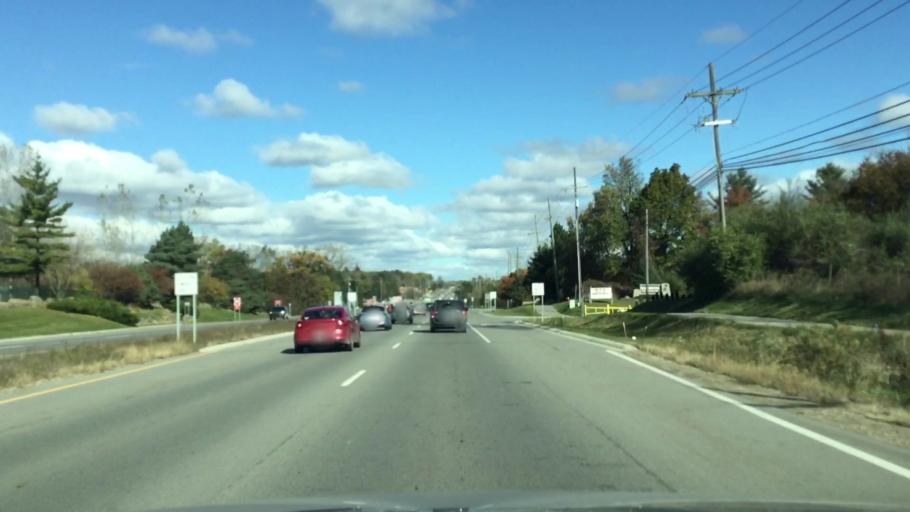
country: US
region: Michigan
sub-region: Oakland County
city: Auburn Hills
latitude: 42.7328
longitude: -83.2442
